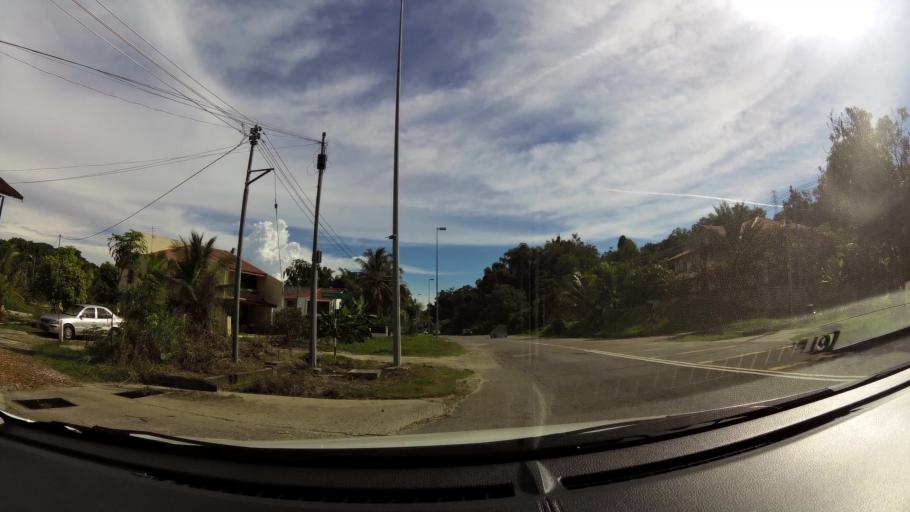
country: BN
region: Brunei and Muara
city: Bandar Seri Begawan
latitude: 5.0225
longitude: 115.0404
